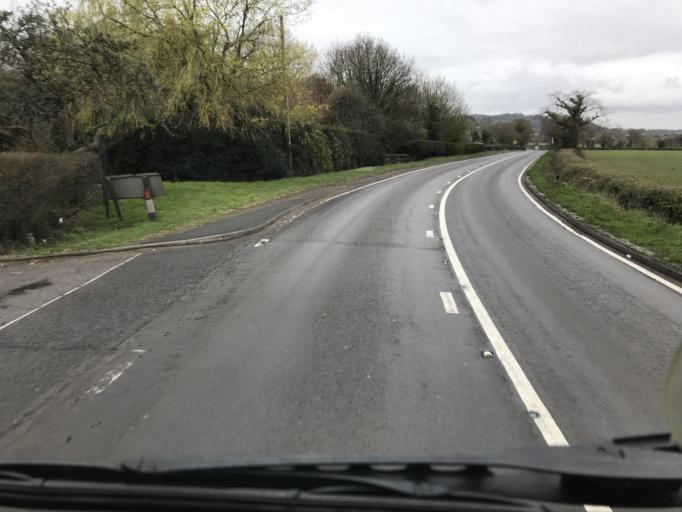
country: GB
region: England
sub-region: Cheshire West and Chester
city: Tattenhall
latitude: 53.1051
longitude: -2.7787
